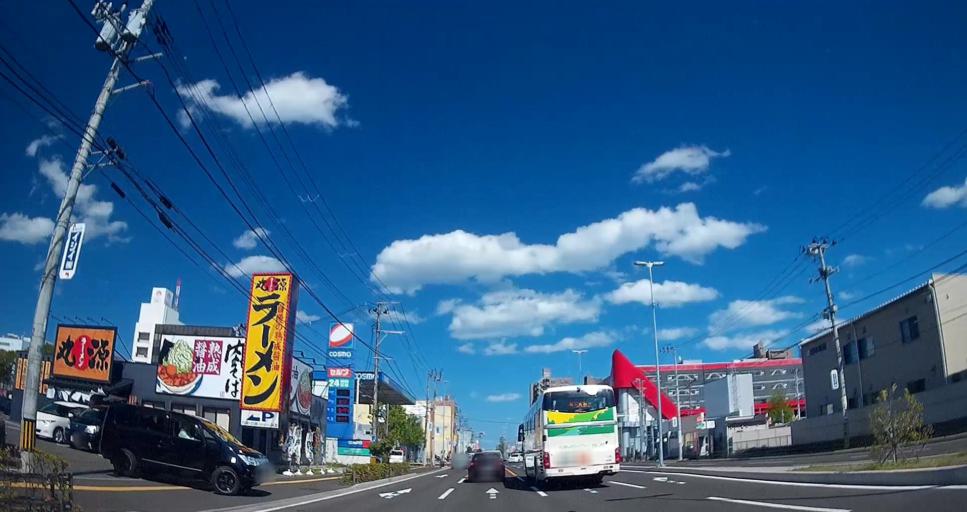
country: JP
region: Miyagi
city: Sendai-shi
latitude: 38.2517
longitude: 140.9198
